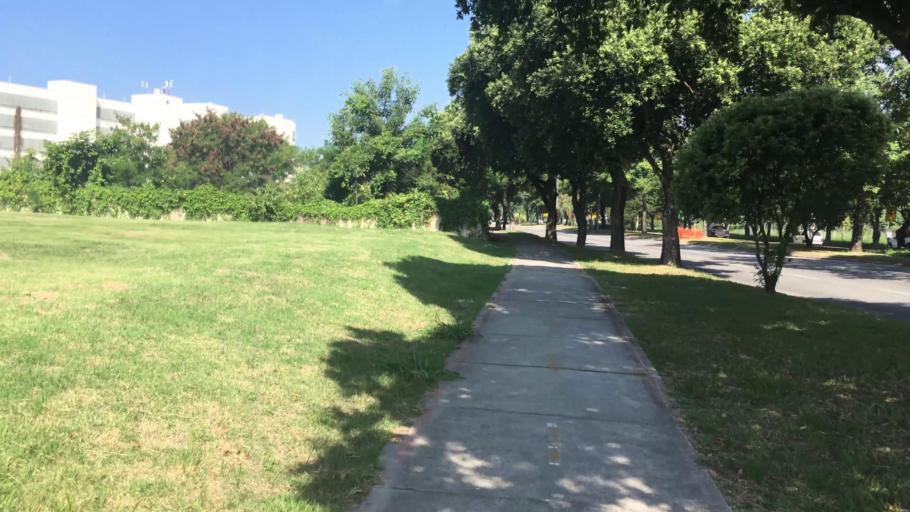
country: BR
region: Rio de Janeiro
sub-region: Rio De Janeiro
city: Rio de Janeiro
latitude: -22.8455
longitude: -43.2356
